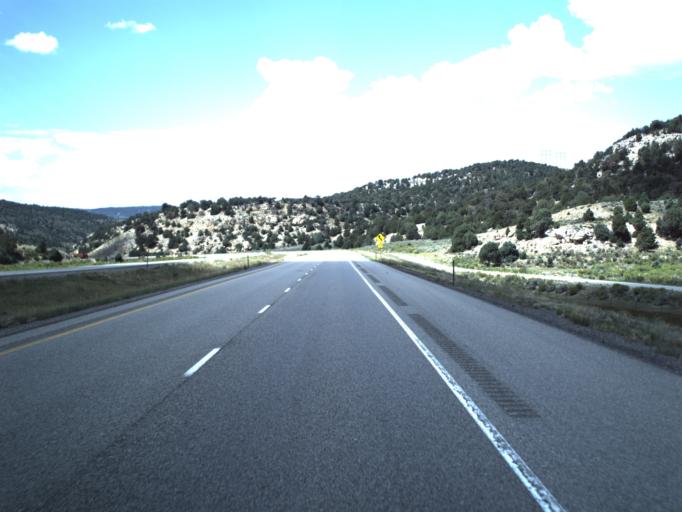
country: US
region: Utah
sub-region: Sevier County
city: Salina
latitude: 38.7991
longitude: -111.5132
